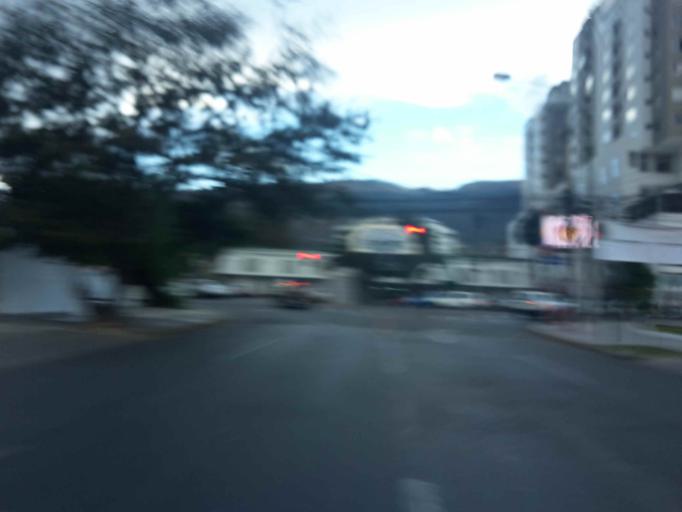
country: BO
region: Cochabamba
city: Cochabamba
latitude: -17.3737
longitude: -66.1511
